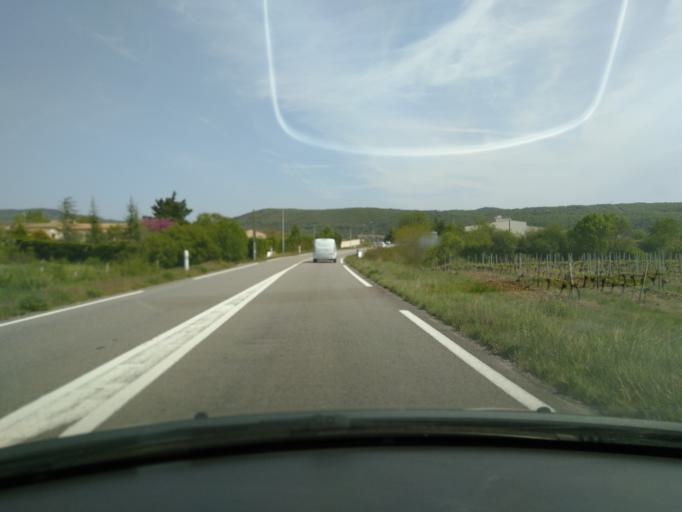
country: FR
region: Rhone-Alpes
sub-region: Departement de l'Ardeche
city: Alba-la-Romaine
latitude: 44.5675
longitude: 4.5984
